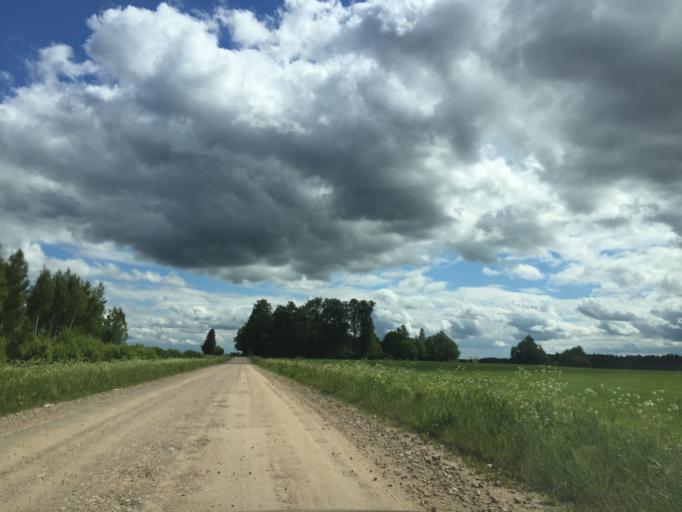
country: LV
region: Vecumnieki
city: Vecumnieki
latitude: 56.4825
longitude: 24.4147
